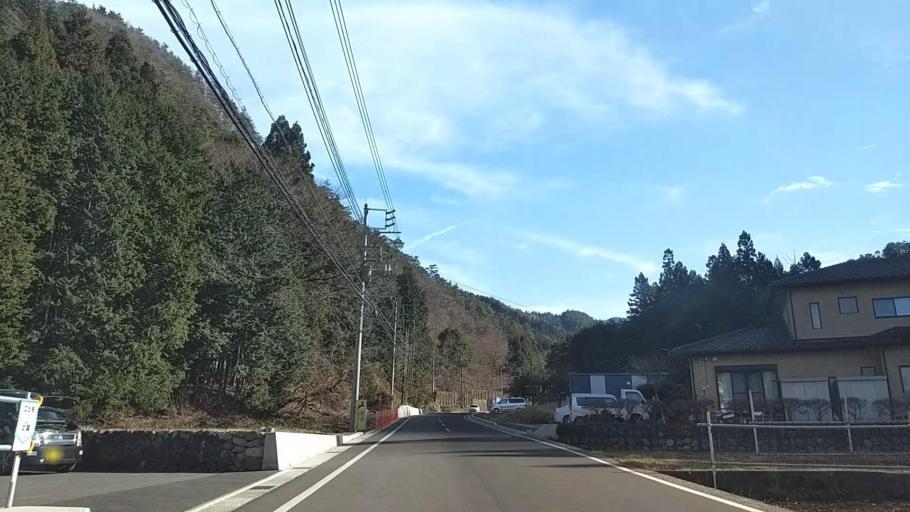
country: JP
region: Yamanashi
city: Otsuki
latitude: 35.5273
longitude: 138.9219
